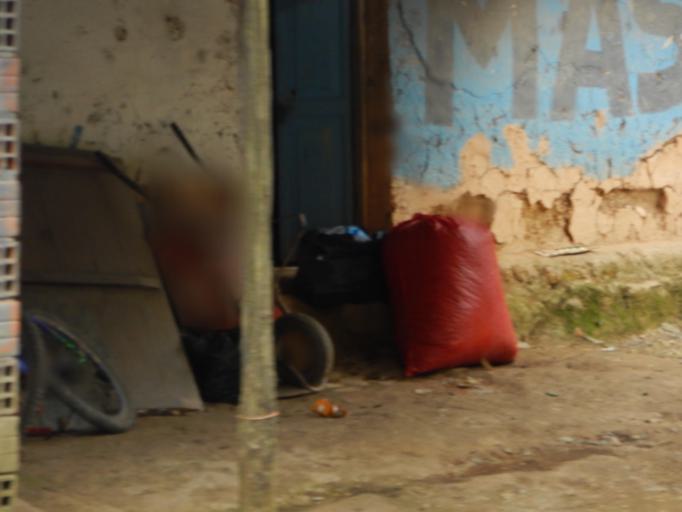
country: BO
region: La Paz
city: Coroico
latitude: -16.1168
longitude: -67.7658
